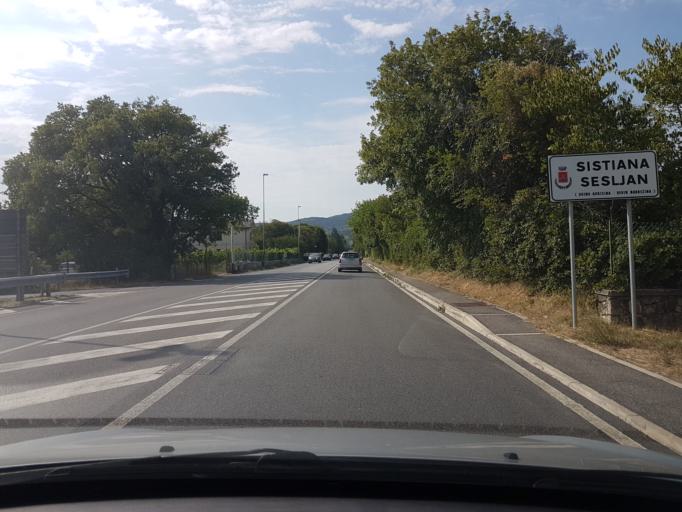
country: IT
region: Friuli Venezia Giulia
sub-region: Provincia di Trieste
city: Sistiana-Visogliano
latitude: 45.7637
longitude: 13.6491
